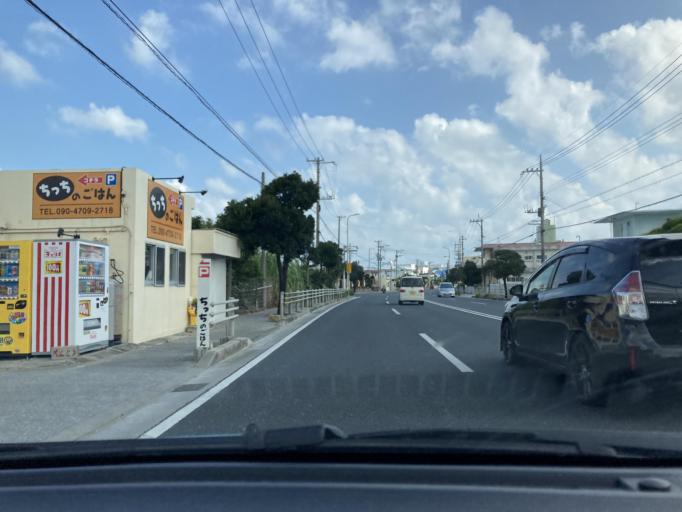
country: JP
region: Okinawa
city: Chatan
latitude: 26.2891
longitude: 127.8134
